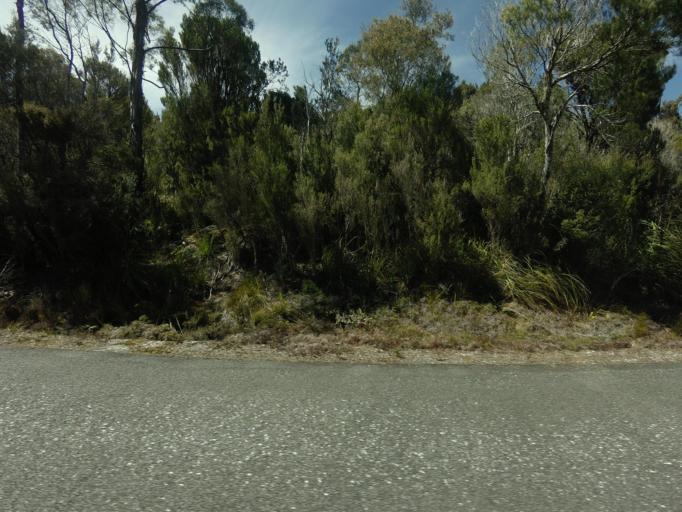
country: AU
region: Tasmania
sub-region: West Coast
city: Queenstown
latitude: -42.7744
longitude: 146.0574
